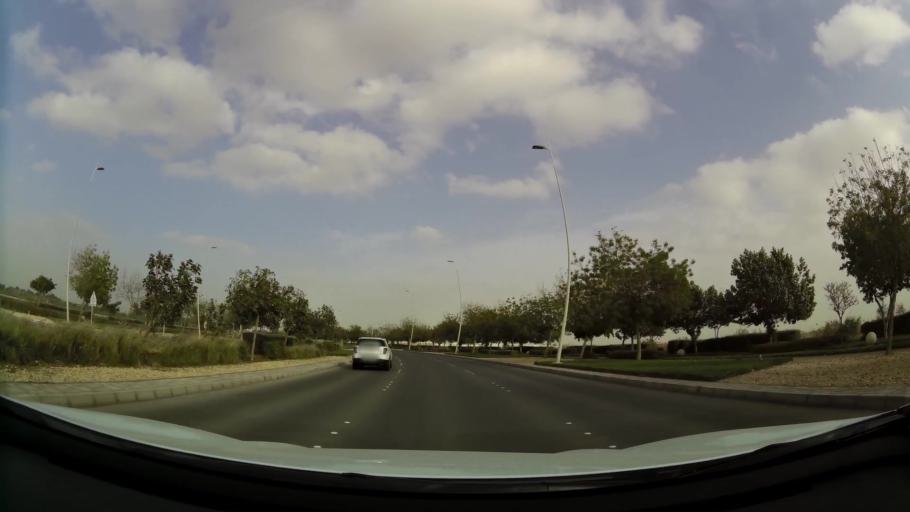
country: AE
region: Abu Dhabi
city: Abu Dhabi
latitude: 24.4826
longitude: 54.6182
